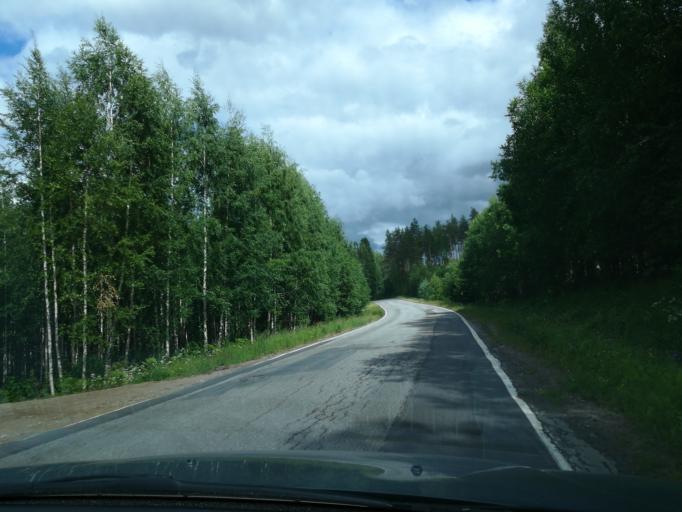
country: FI
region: South Karelia
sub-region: Lappeenranta
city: Savitaipale
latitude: 61.2534
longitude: 27.7079
